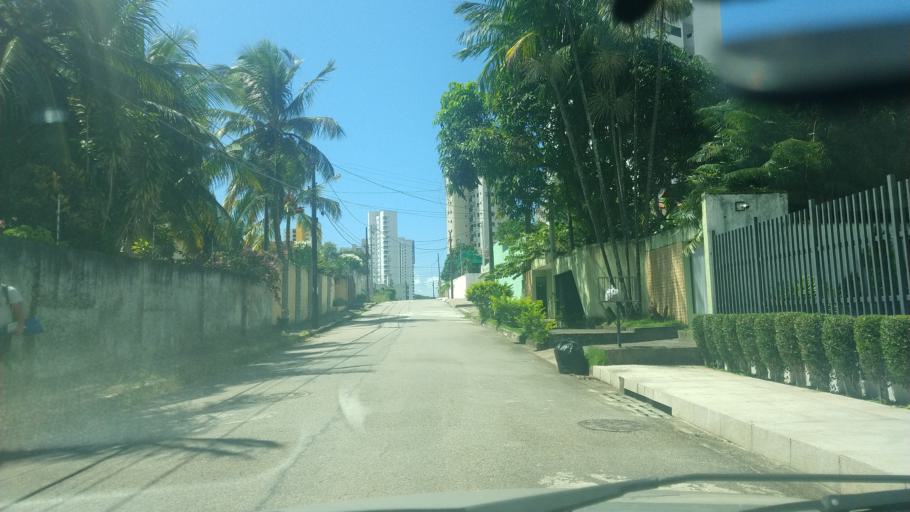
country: BR
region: Rio Grande do Norte
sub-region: Natal
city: Natal
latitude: -5.8630
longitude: -35.2009
